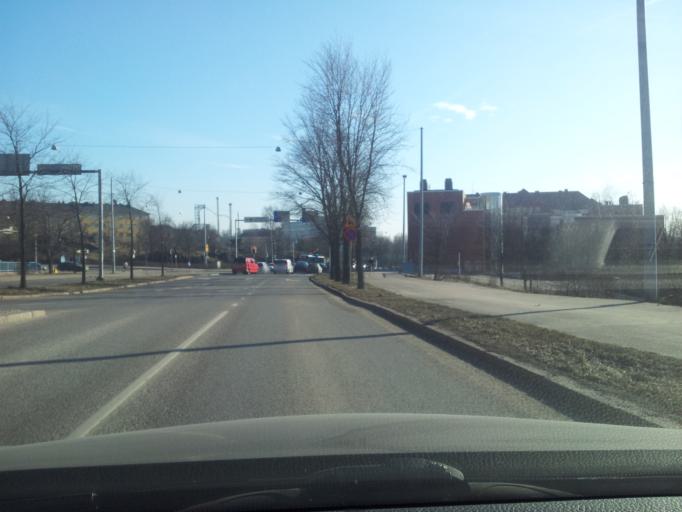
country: FI
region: Uusimaa
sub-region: Helsinki
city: Helsinki
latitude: 60.1965
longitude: 24.9356
